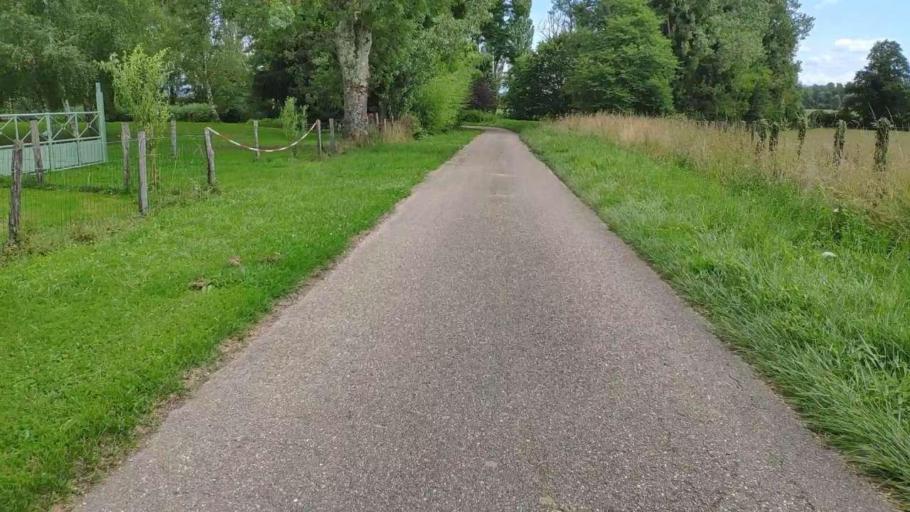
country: FR
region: Franche-Comte
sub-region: Departement du Jura
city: Chaussin
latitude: 46.8679
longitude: 5.4311
